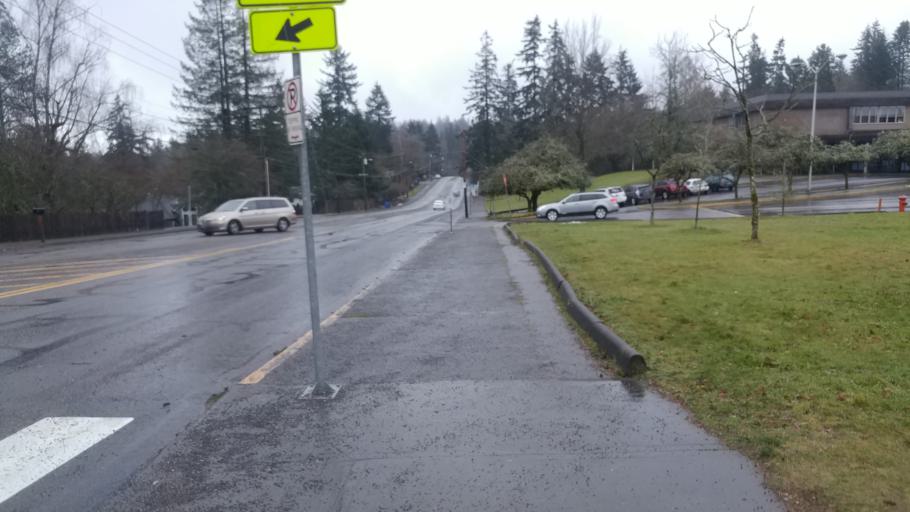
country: US
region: Oregon
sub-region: Washington County
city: Metzger
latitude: 45.4489
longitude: -122.7130
